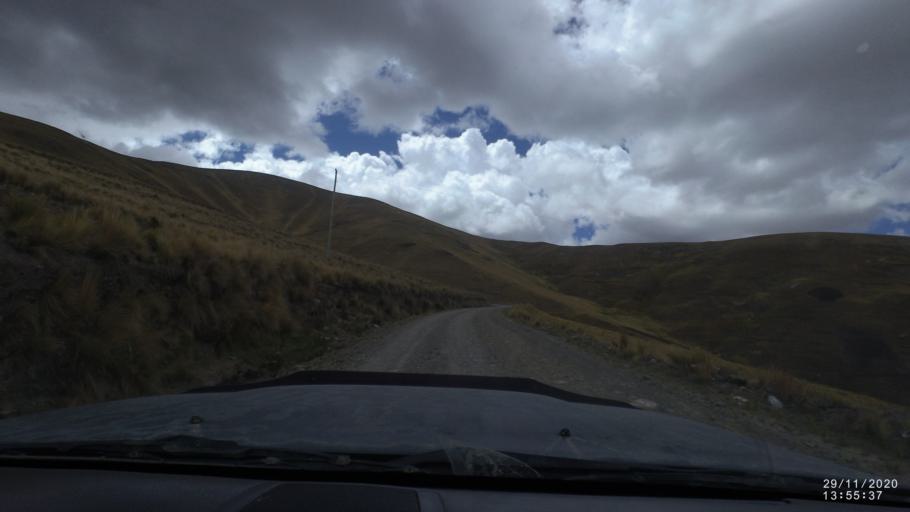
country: BO
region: Cochabamba
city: Sipe Sipe
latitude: -17.1748
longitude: -66.3584
